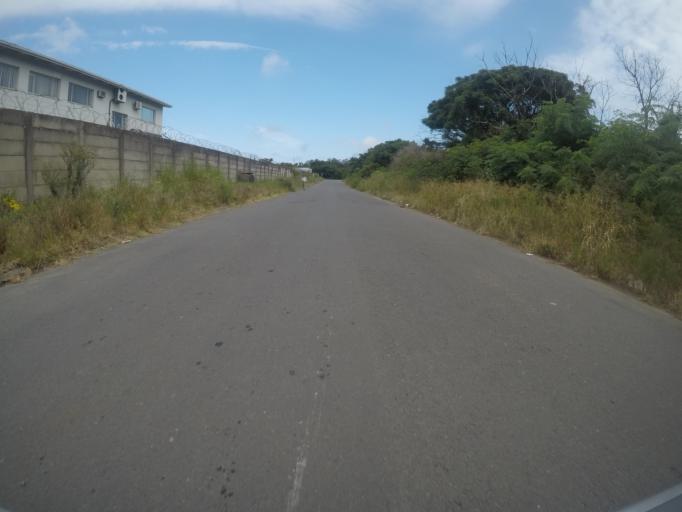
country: ZA
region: Eastern Cape
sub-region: Buffalo City Metropolitan Municipality
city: East London
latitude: -32.9894
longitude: 27.8879
